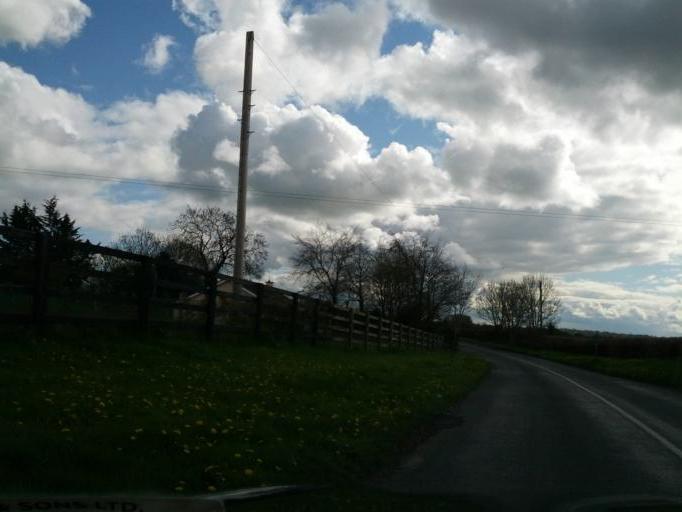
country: IE
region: Leinster
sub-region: An Mhi
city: Dunshaughlin
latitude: 53.5210
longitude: -6.6509
